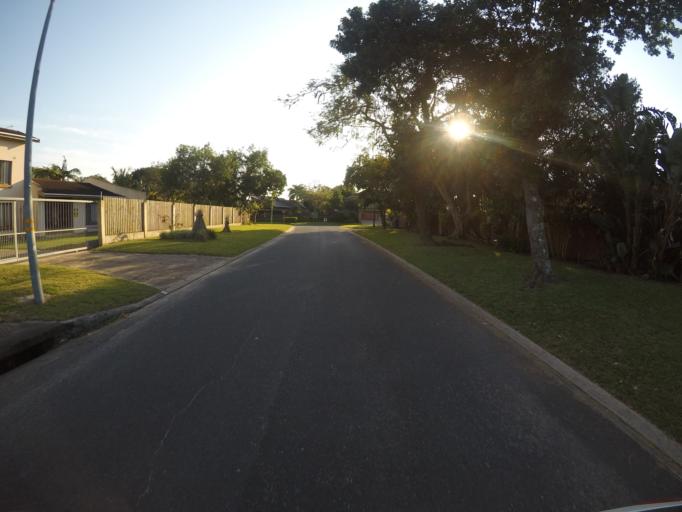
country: ZA
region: KwaZulu-Natal
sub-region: uThungulu District Municipality
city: Richards Bay
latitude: -28.7730
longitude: 32.1151
